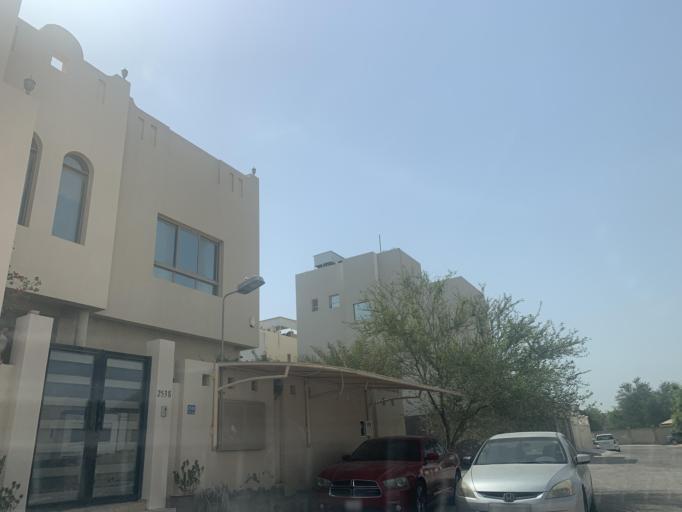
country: BH
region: Northern
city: Madinat `Isa
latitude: 26.1865
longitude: 50.4936
